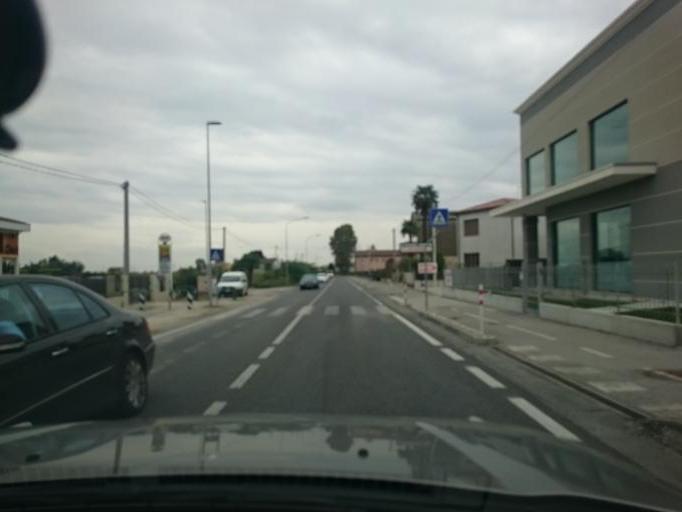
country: IT
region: Veneto
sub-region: Provincia di Padova
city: Arzergrande
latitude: 45.2712
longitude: 12.0280
